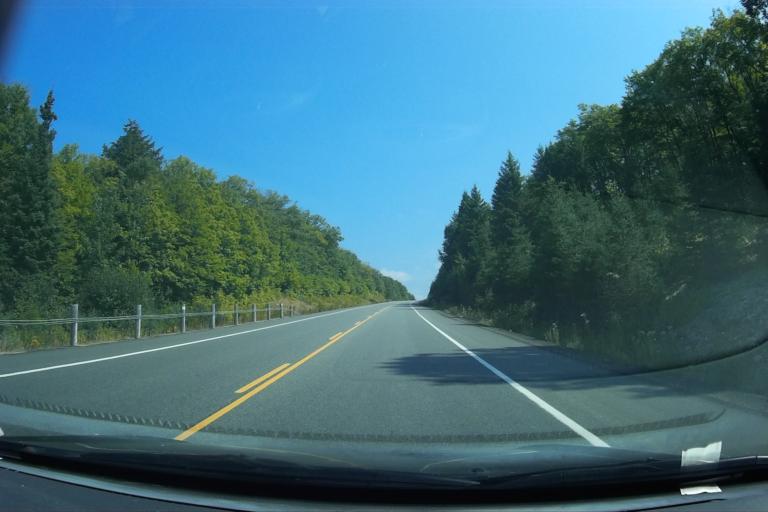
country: CA
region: Ontario
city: Huntsville
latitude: 45.5427
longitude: -78.6885
